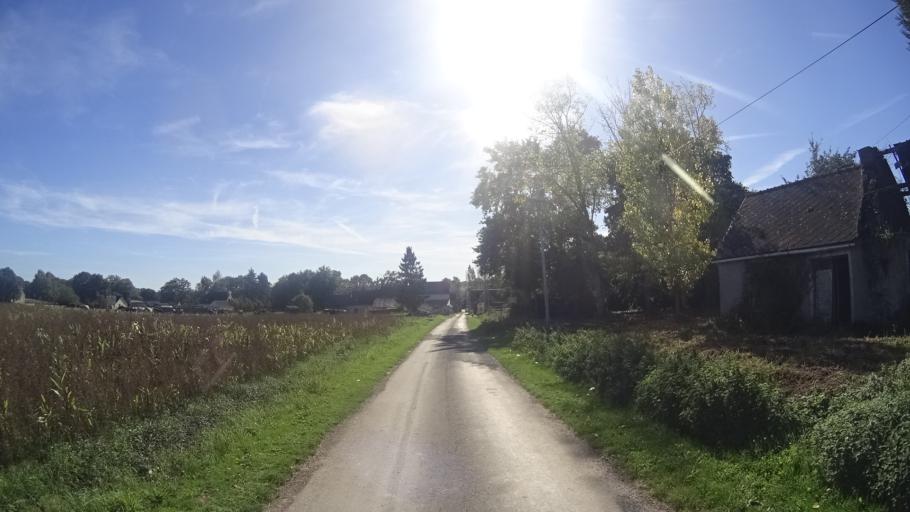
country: FR
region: Brittany
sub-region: Departement du Morbihan
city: Peillac
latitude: 47.7338
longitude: -2.1816
